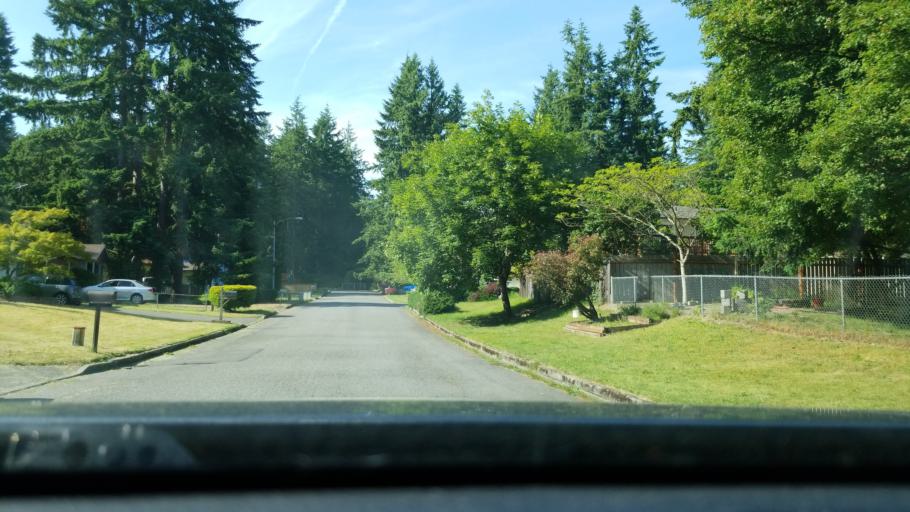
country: US
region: Washington
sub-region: King County
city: Fairwood
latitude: 47.4767
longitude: -122.1456
